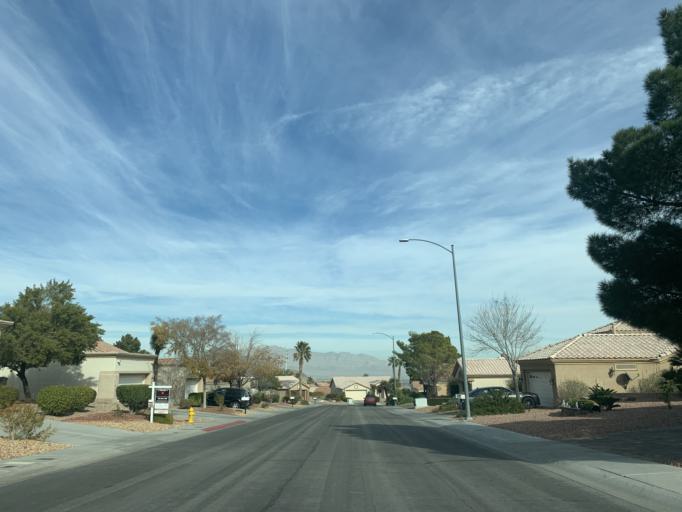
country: US
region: Nevada
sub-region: Clark County
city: Summerlin South
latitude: 36.2161
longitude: -115.3290
